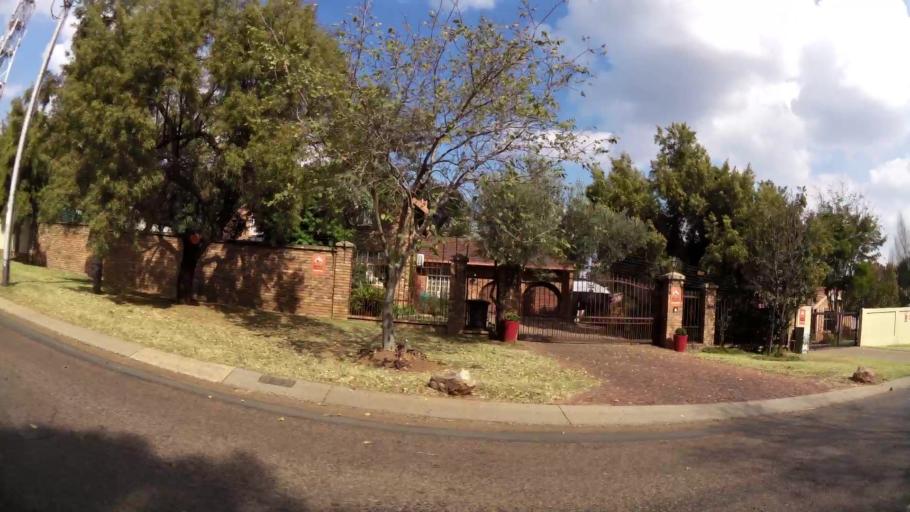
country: ZA
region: Gauteng
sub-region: City of Tshwane Metropolitan Municipality
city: Centurion
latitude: -25.8397
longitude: 28.2697
